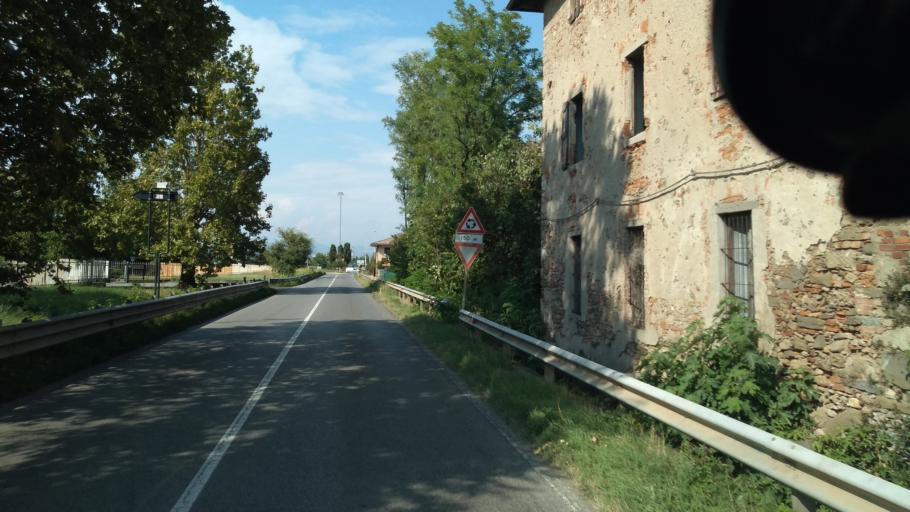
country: IT
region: Lombardy
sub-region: Provincia di Bergamo
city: Arcene
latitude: 45.5657
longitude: 9.6103
